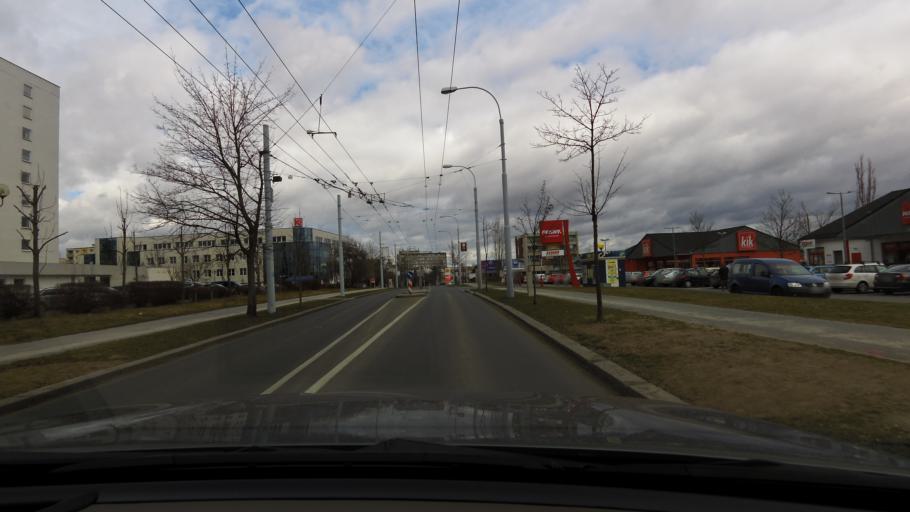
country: CZ
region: Plzensky
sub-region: Okres Plzen-Mesto
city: Pilsen
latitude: 49.7259
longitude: 13.3778
